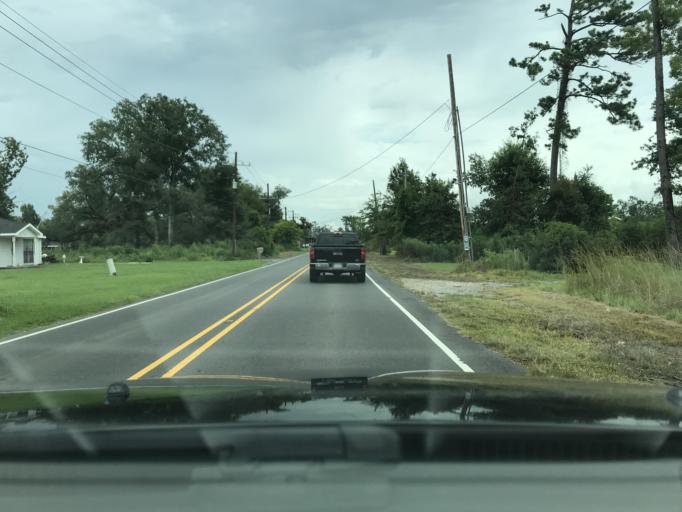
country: US
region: Louisiana
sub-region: Calcasieu Parish
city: Moss Bluff
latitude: 30.3007
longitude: -93.1922
